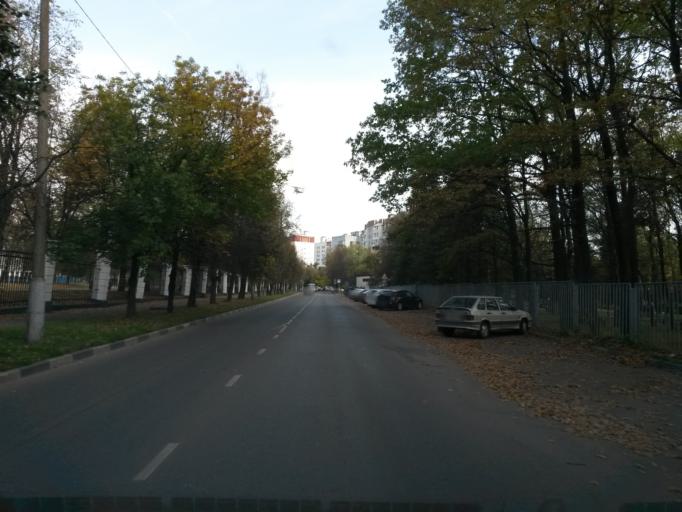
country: RU
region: Moskovskaya
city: Mosrentgen
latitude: 55.6110
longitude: 37.4668
